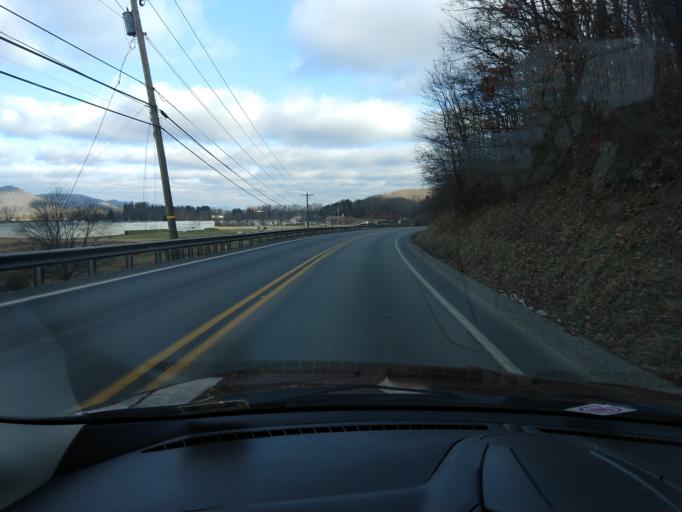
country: US
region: West Virginia
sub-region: Randolph County
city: Elkins
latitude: 38.8203
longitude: -79.8757
